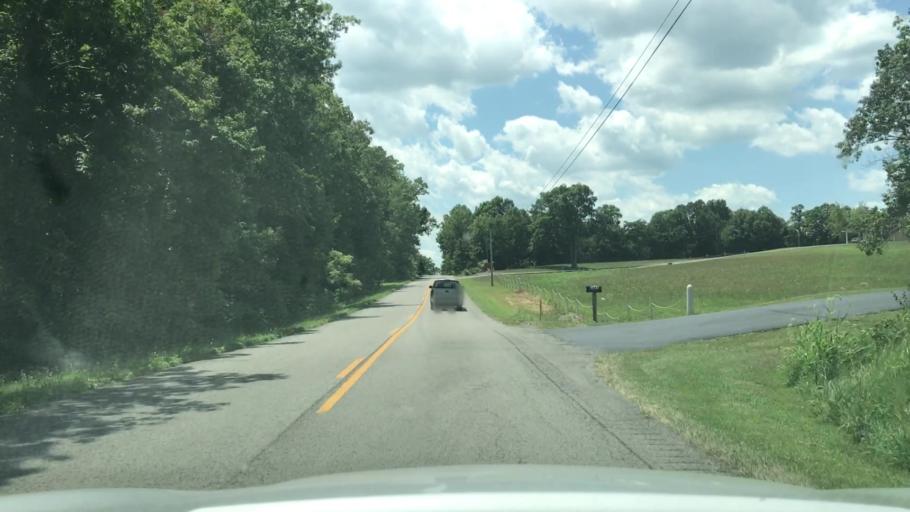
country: US
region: Kentucky
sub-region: Muhlenberg County
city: Greenville
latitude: 37.1842
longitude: -87.2284
